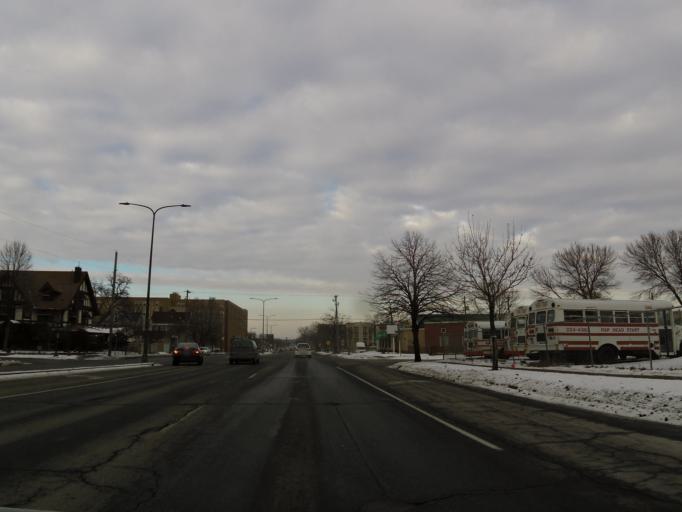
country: US
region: Minnesota
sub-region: Ramsey County
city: Saint Paul
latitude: 44.9535
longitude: -93.1262
